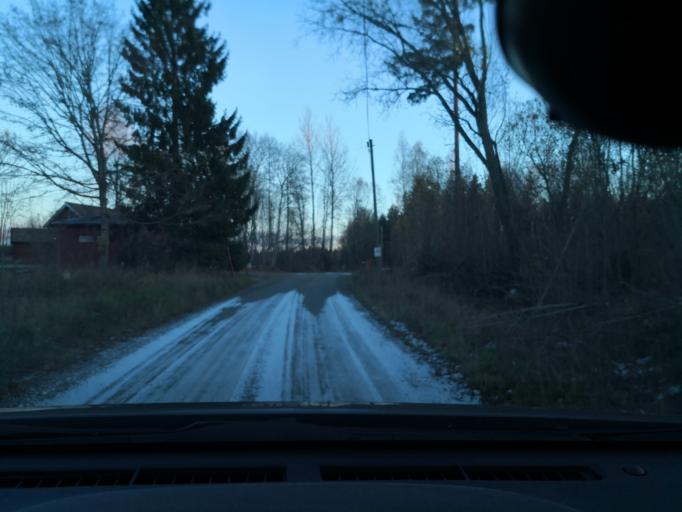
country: SE
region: Vaestmanland
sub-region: Vasteras
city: Tillberga
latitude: 59.7674
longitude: 16.6082
